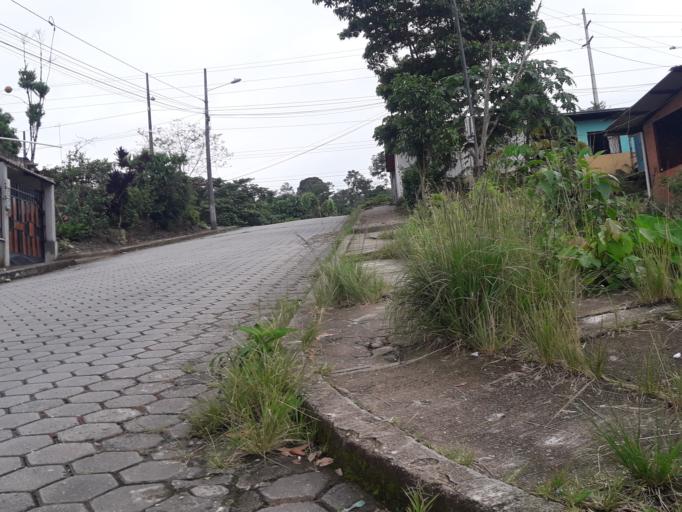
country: EC
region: Napo
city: Tena
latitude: -1.0010
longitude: -77.8075
